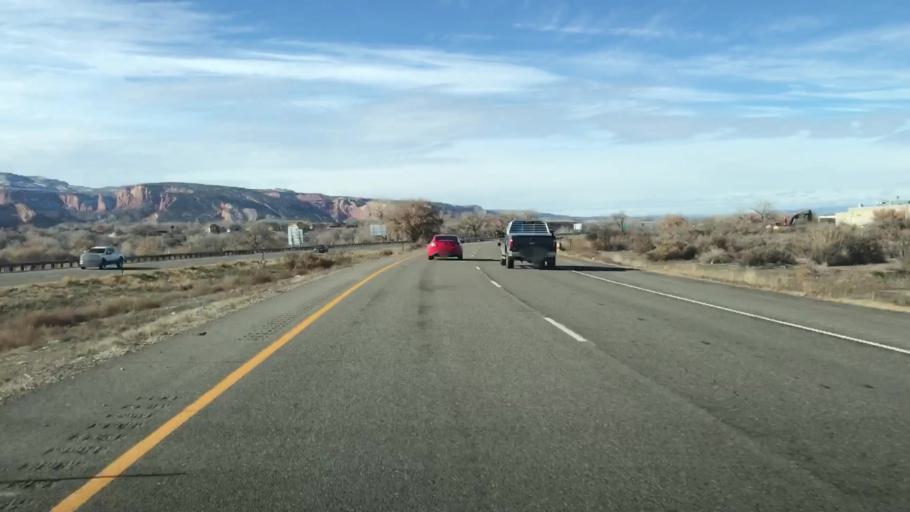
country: US
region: Colorado
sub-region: Mesa County
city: Redlands
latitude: 39.1094
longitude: -108.6548
